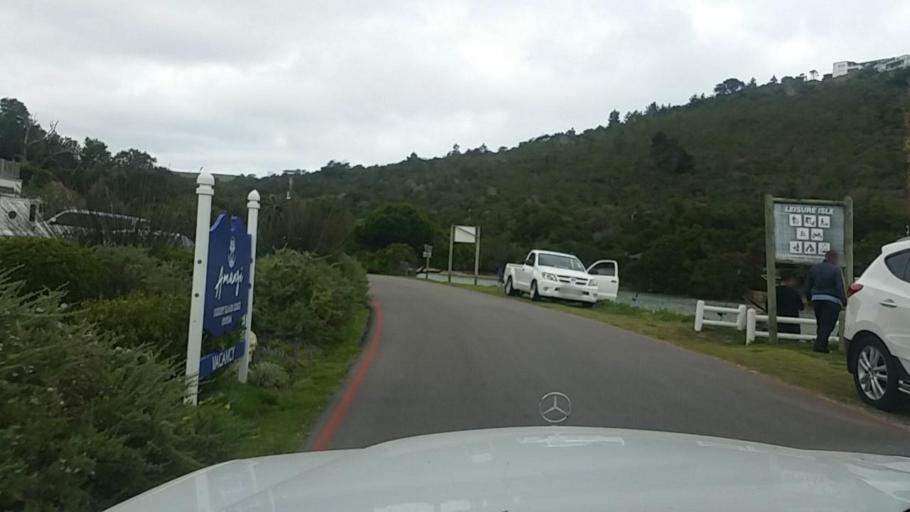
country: ZA
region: Western Cape
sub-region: Eden District Municipality
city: Knysna
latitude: -34.0722
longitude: 23.0638
